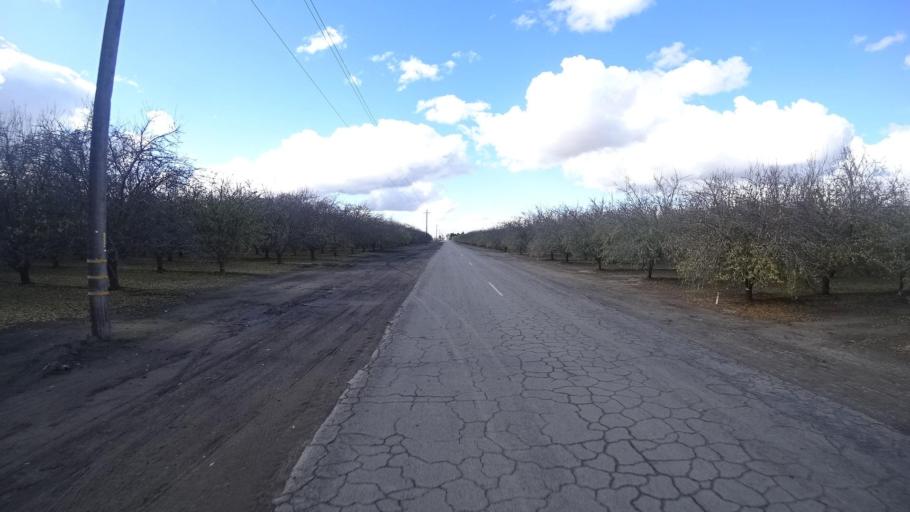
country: US
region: California
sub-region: Kern County
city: Greenfield
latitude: 35.2234
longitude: -119.0671
